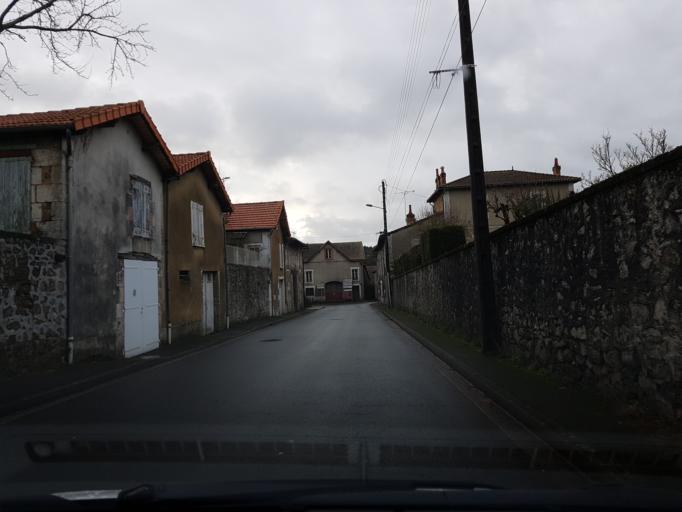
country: FR
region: Poitou-Charentes
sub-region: Departement de la Charente
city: Chabanais
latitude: 45.8780
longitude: 0.7222
